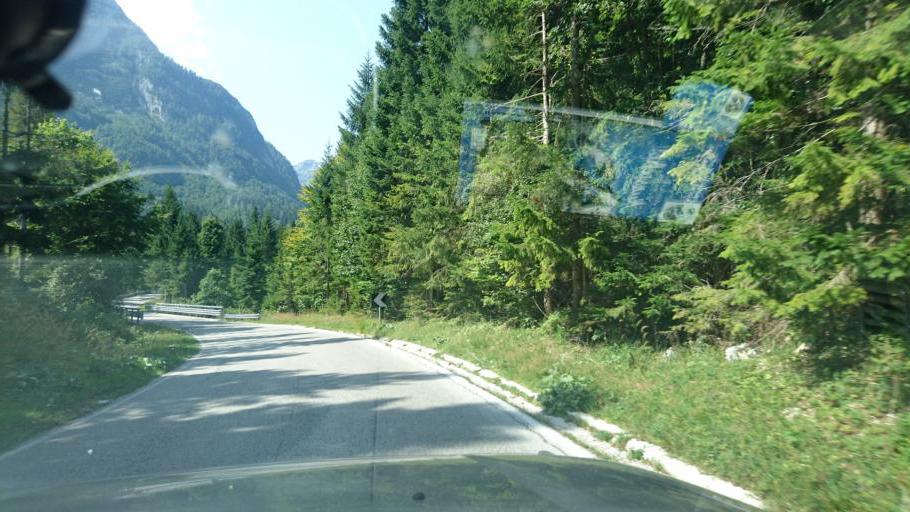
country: SI
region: Bovec
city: Bovec
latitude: 46.3976
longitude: 13.5028
